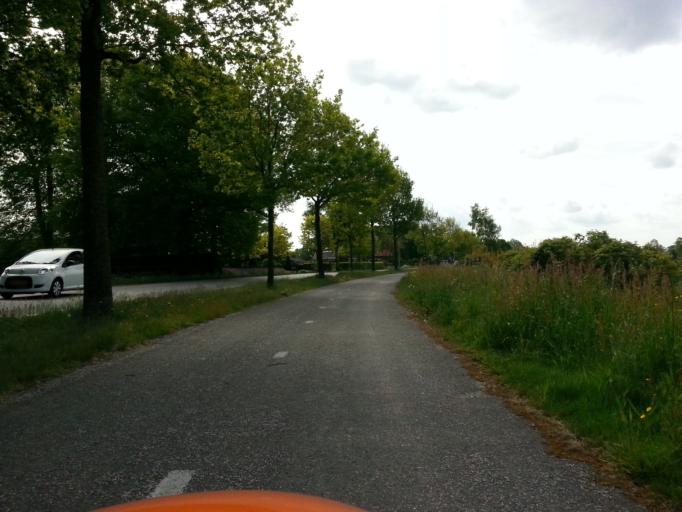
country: NL
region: Gelderland
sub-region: Gemeente Ede
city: Lunteren
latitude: 52.0871
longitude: 5.6041
